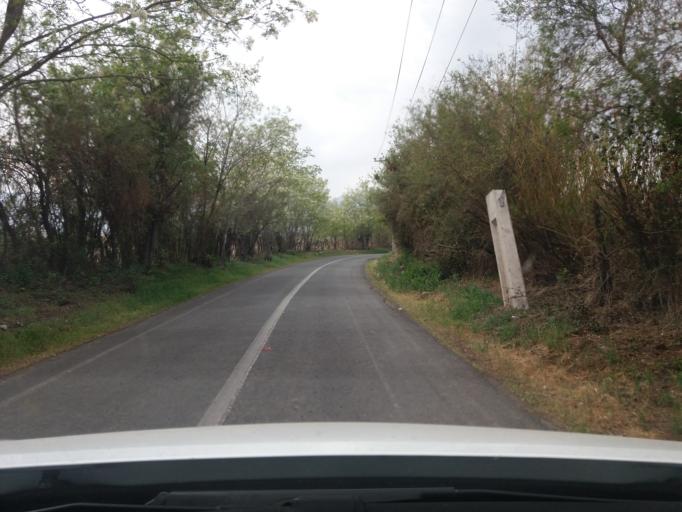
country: CL
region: Valparaiso
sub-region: Provincia de Los Andes
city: Los Andes
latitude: -32.8279
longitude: -70.6360
